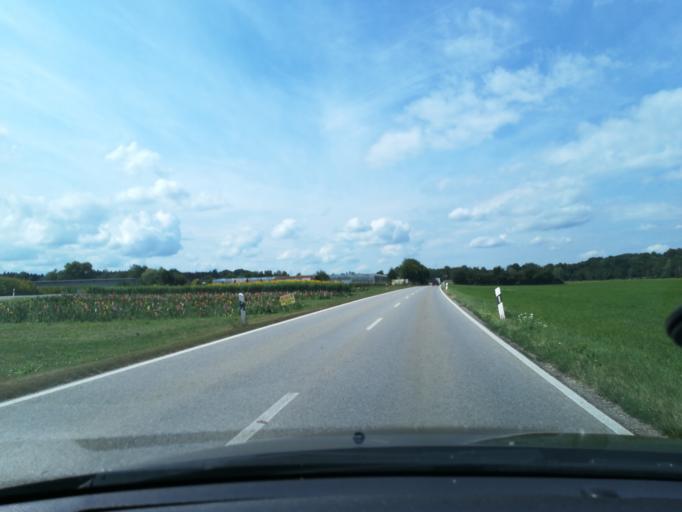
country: DE
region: Bavaria
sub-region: Upper Bavaria
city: Grafing bei Munchen
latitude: 48.0403
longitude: 11.9549
